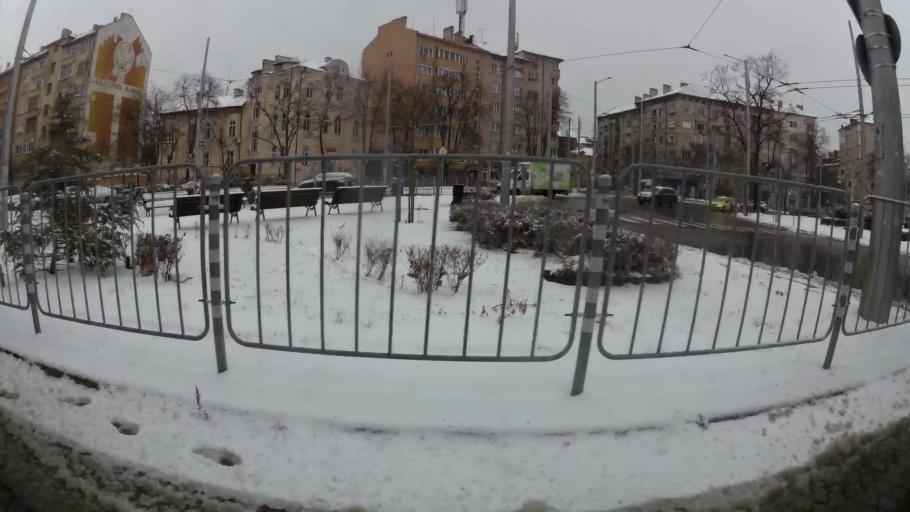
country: BG
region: Sofia-Capital
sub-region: Stolichna Obshtina
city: Sofia
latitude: 42.6926
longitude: 23.3108
